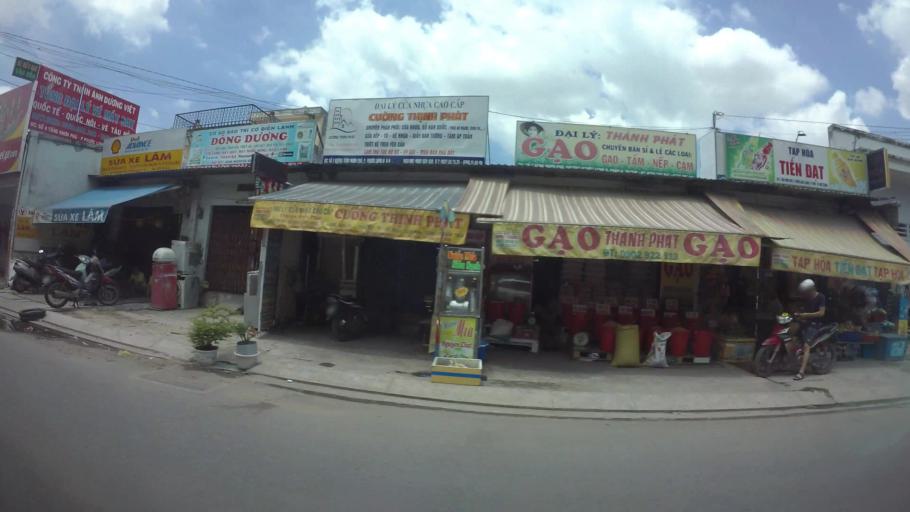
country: VN
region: Ho Chi Minh City
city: Quan Chin
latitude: 10.8276
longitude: 106.7687
